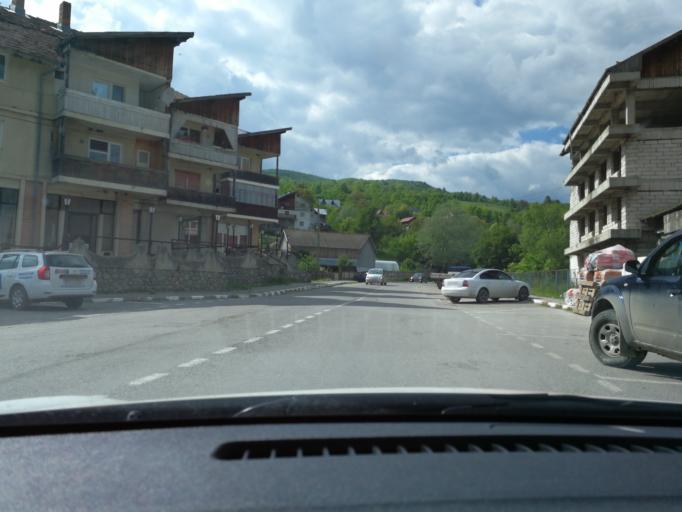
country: RO
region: Prahova
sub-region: Comuna Valea Doftanei
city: Tesila
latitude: 45.3039
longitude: 25.7215
